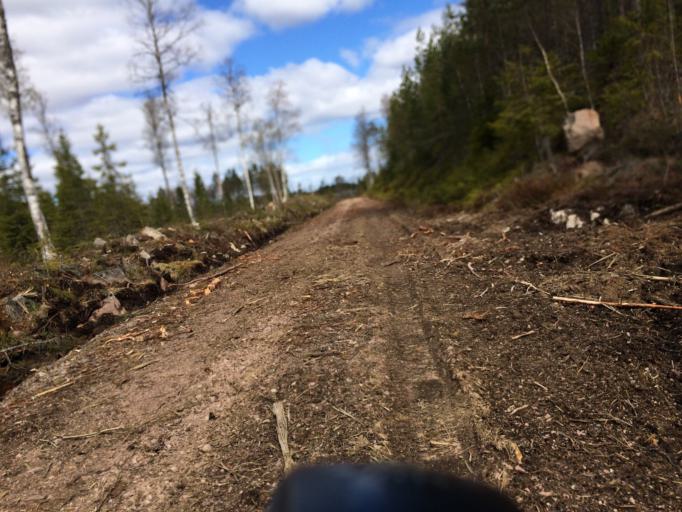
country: SE
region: OErebro
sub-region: Hallefors Kommun
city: Haellefors
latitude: 60.0491
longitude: 14.5255
